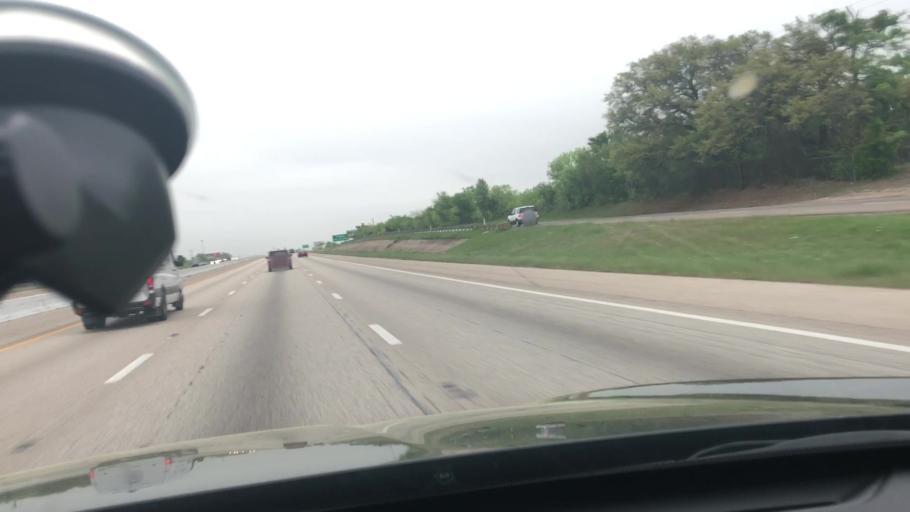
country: US
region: Texas
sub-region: Bell County
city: Belton
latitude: 31.0692
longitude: -97.4255
